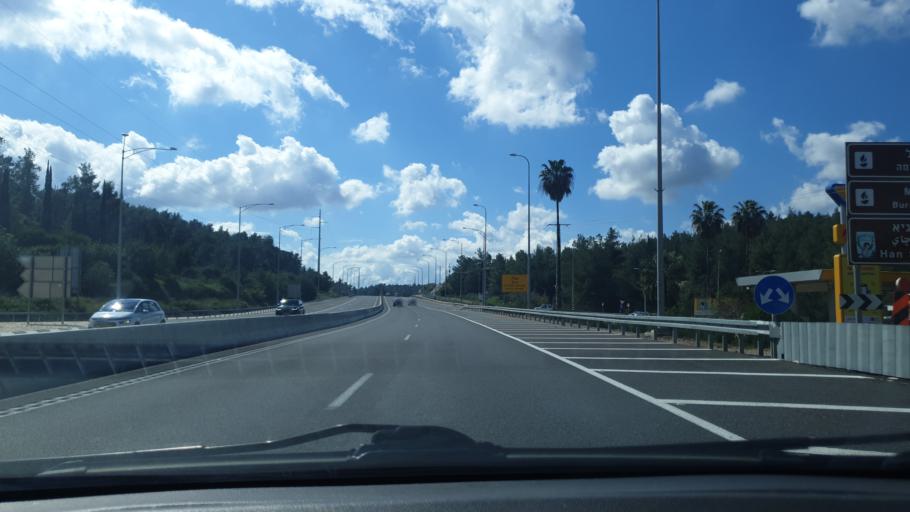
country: IL
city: Mevo horon
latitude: 31.8086
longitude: 35.0186
